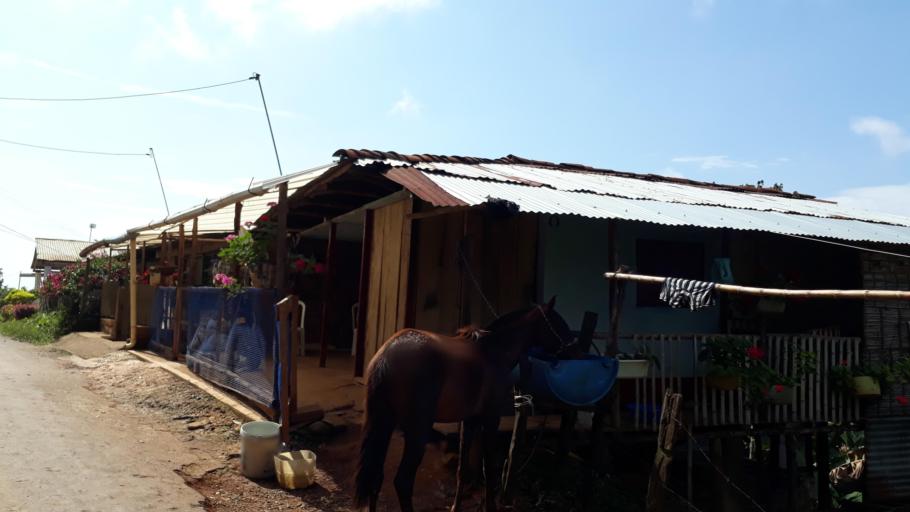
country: CO
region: Valle del Cauca
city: Jamundi
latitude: 3.2688
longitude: -76.6264
